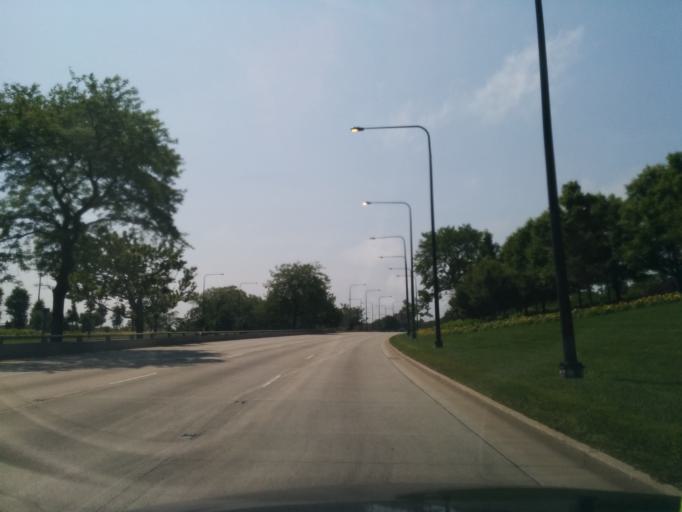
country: US
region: Illinois
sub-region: Cook County
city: Chicago
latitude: 41.8382
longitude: -87.6086
